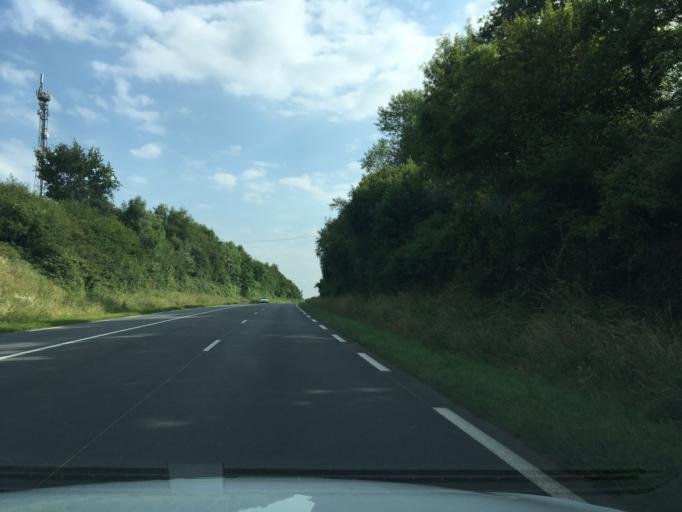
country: FR
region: Poitou-Charentes
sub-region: Departement des Deux-Sevres
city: Saint-Pardoux
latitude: 46.5782
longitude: -0.2933
